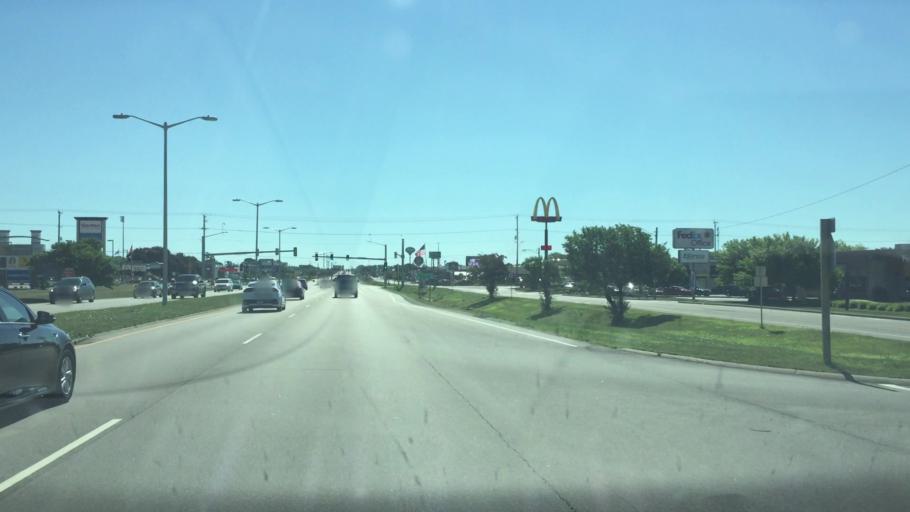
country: US
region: Wisconsin
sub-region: Outagamie County
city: Appleton
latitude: 44.2617
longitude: -88.4583
